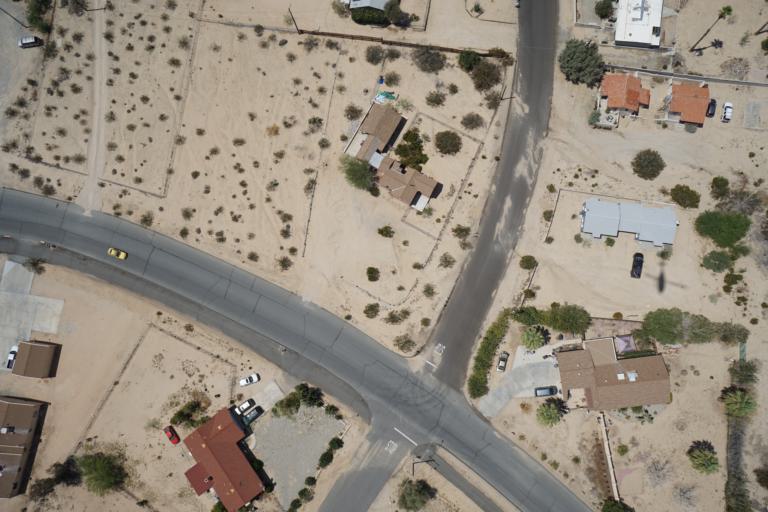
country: US
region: California
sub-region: San Bernardino County
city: Twentynine Palms
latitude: 34.1489
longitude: -116.0577
